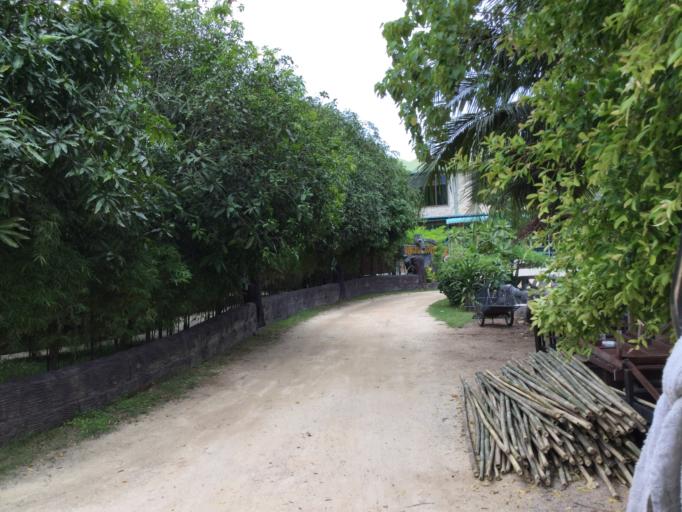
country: TH
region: Nakhon Si Thammarat
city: Ko Pha Ngan
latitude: 9.7706
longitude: 100.0565
